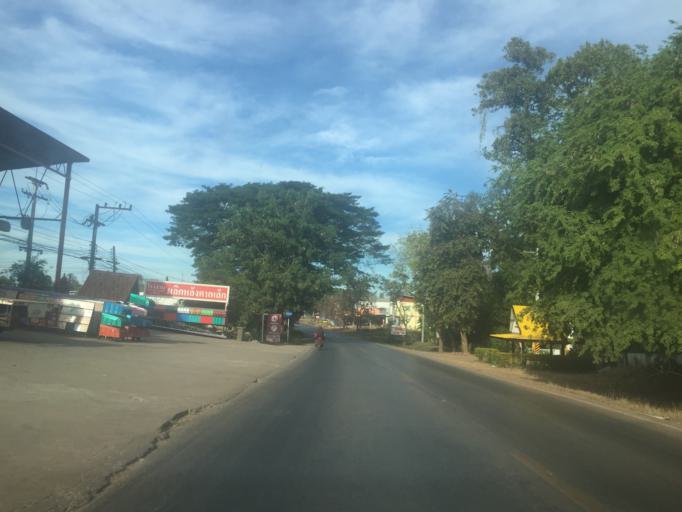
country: TH
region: Changwat Udon Thani
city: Si That
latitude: 16.9736
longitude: 103.2280
